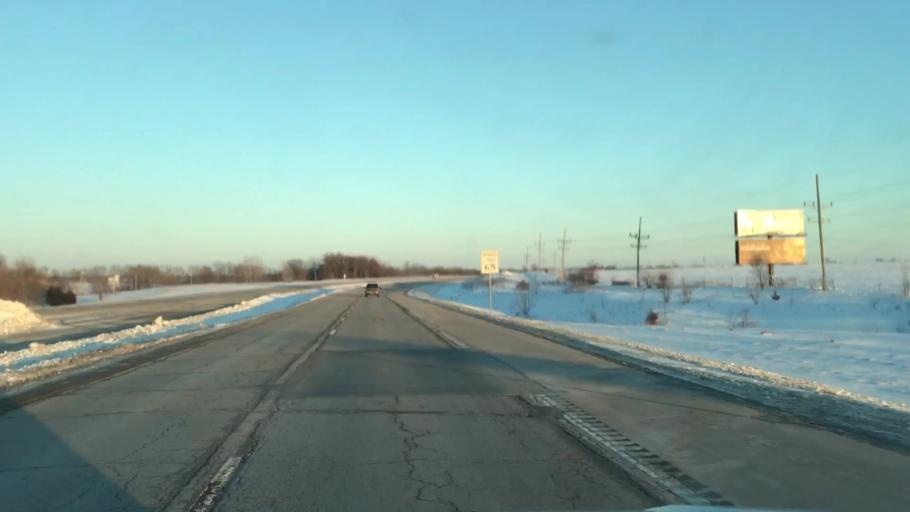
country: US
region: Missouri
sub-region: Clinton County
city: Cameron
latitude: 39.7615
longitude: -94.3560
